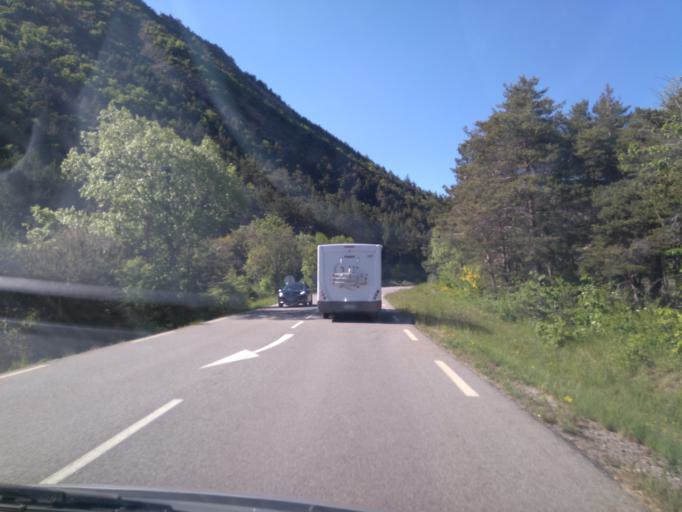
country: FR
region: Provence-Alpes-Cote d'Azur
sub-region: Departement des Hautes-Alpes
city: Veynes
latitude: 44.5428
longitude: 5.7784
